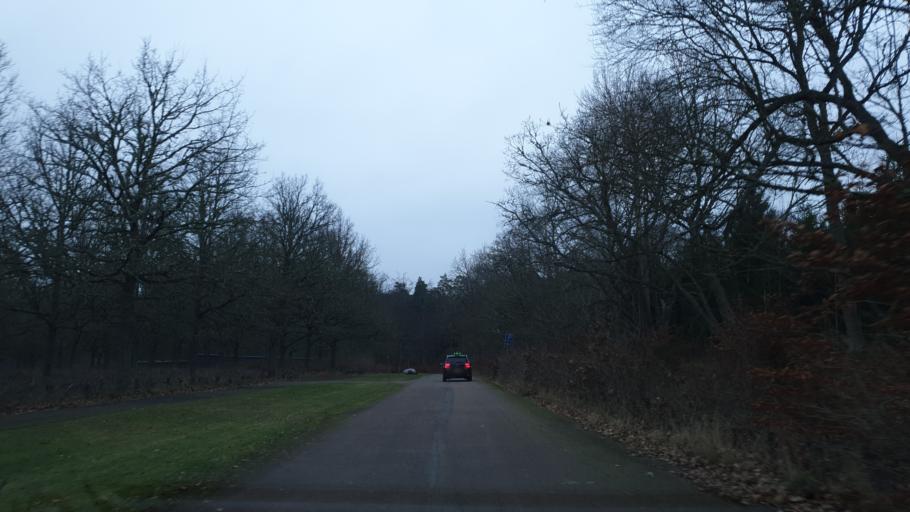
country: SE
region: Blekinge
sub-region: Karlskrona Kommun
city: Rodeby
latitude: 56.2131
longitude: 15.6832
